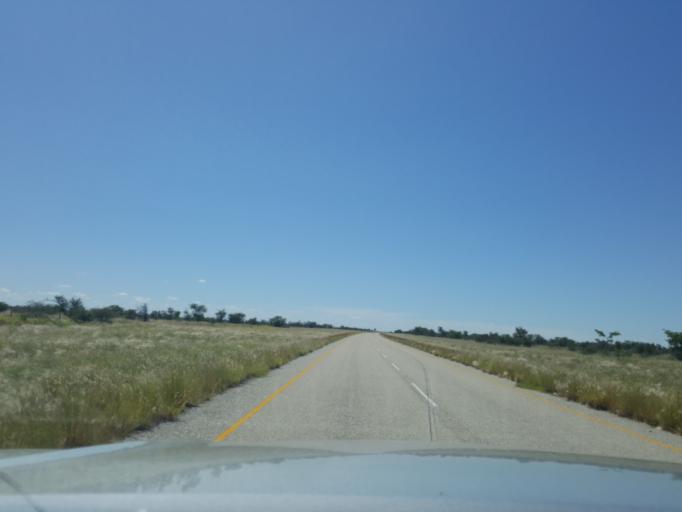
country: BW
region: Central
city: Gweta
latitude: -20.2215
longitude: 25.0274
